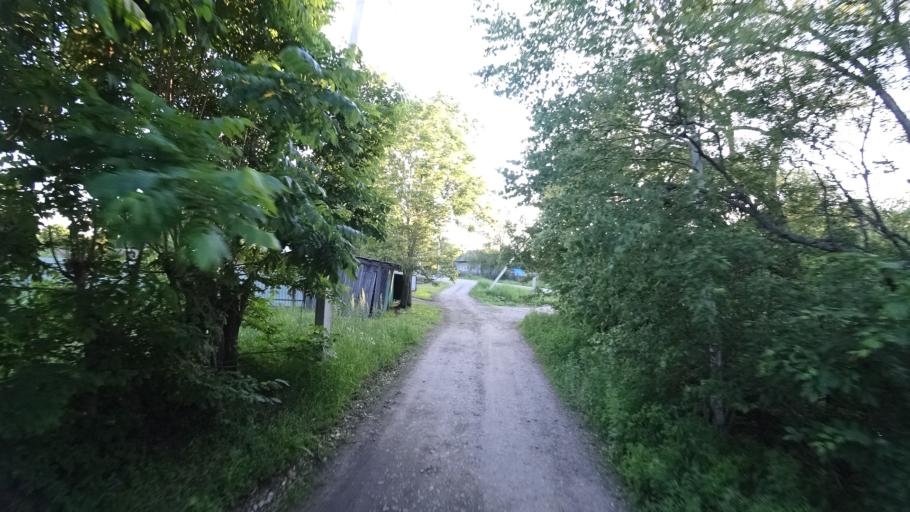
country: RU
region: Khabarovsk Krai
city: Khor
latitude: 47.8564
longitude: 134.9886
